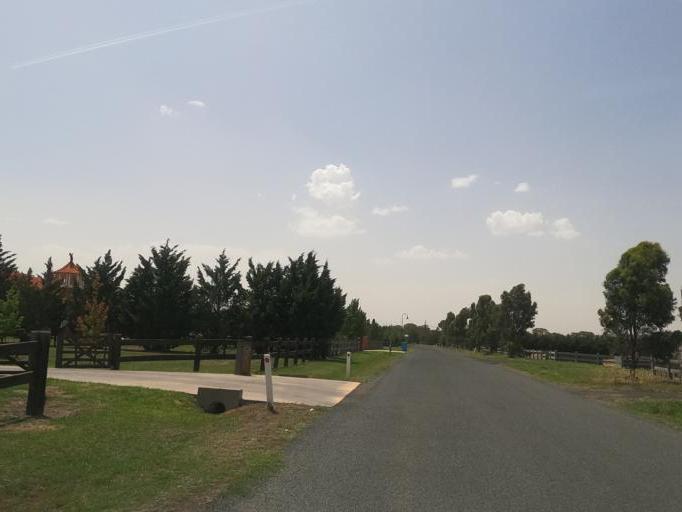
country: AU
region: Victoria
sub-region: Hume
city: Craigieburn
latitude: -37.5612
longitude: 144.8911
